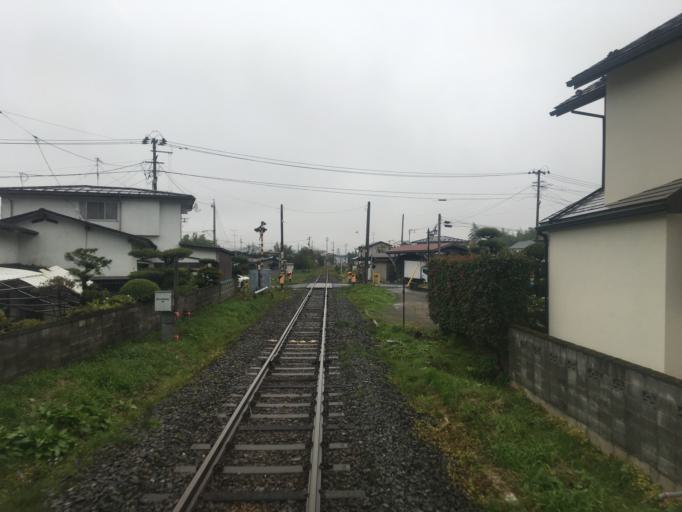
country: JP
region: Miyagi
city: Furukawa
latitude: 38.6571
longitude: 140.8661
